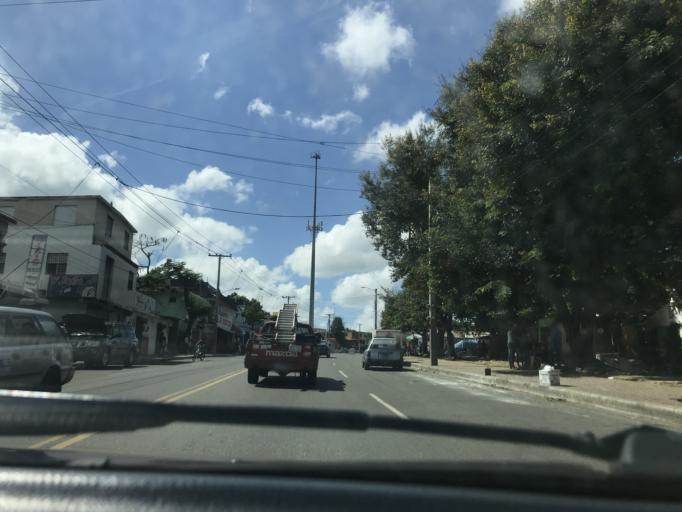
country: DO
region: Santiago
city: Santiago de los Caballeros
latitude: 19.4382
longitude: -70.6991
